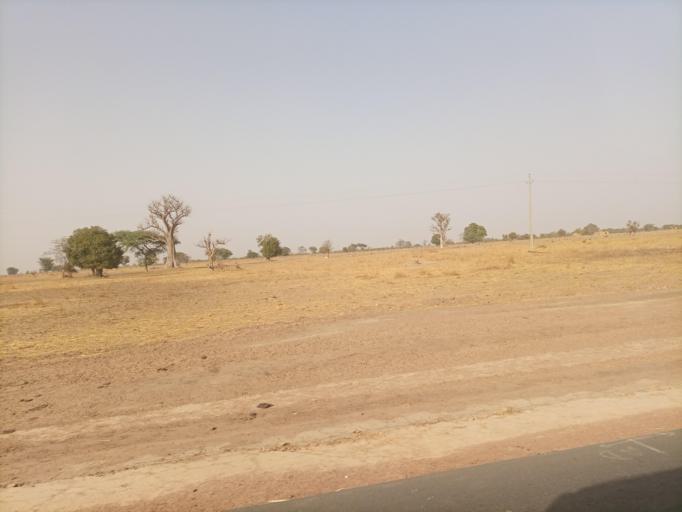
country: SN
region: Fatick
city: Passi
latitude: 14.0274
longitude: -16.3057
